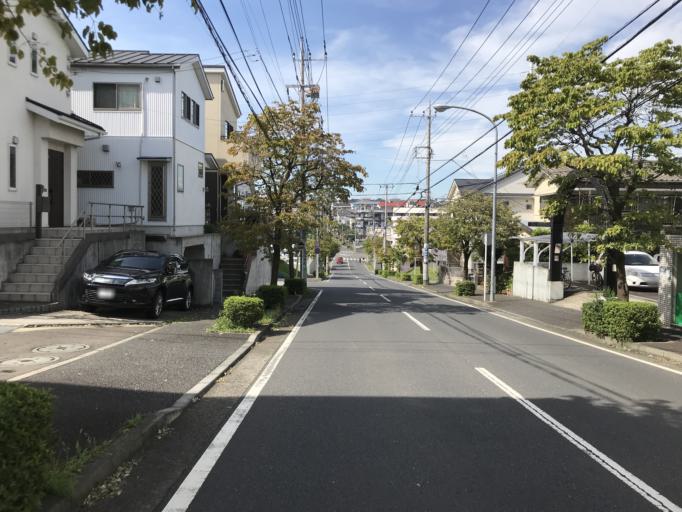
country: JP
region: Tokyo
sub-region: Machida-shi
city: Machida
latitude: 35.5583
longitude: 139.5068
